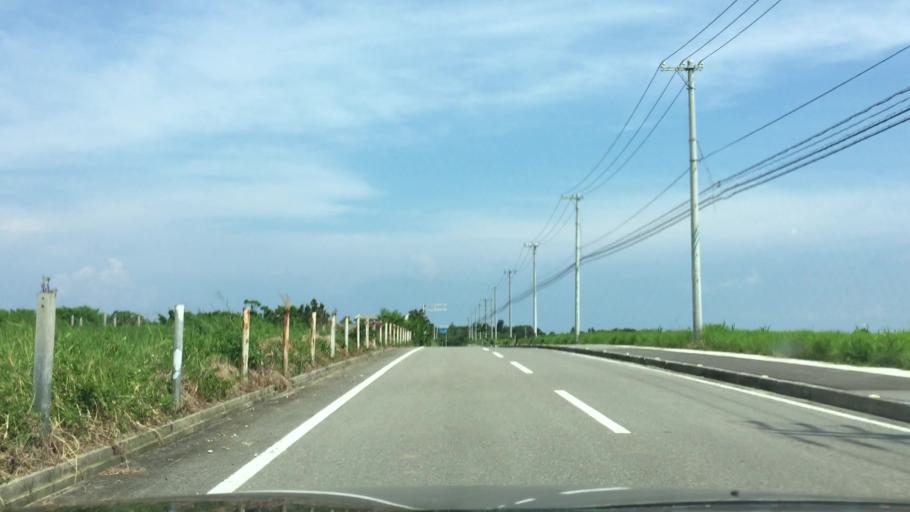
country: JP
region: Okinawa
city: Ishigaki
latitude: 24.5037
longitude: 124.2761
